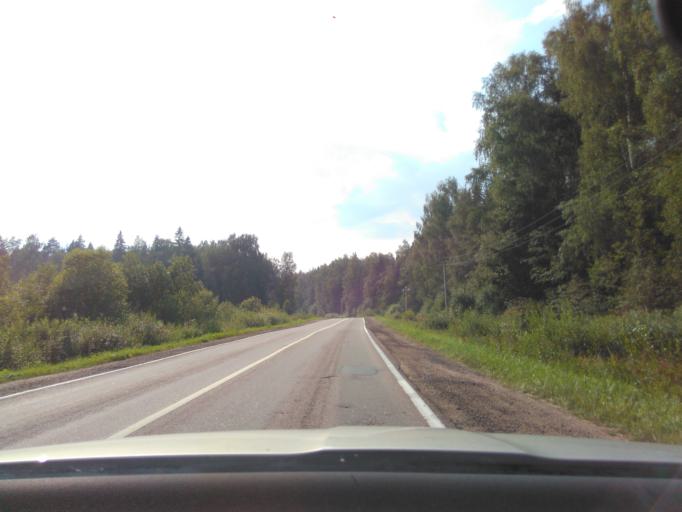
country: RU
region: Moskovskaya
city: Solnechnogorsk
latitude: 56.1462
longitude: 36.8214
